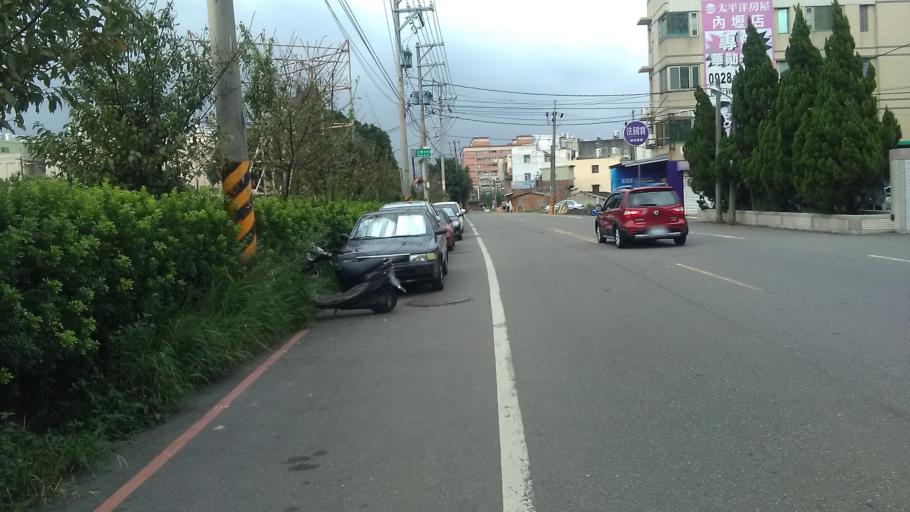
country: TW
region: Taiwan
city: Taoyuan City
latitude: 24.9537
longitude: 121.2612
